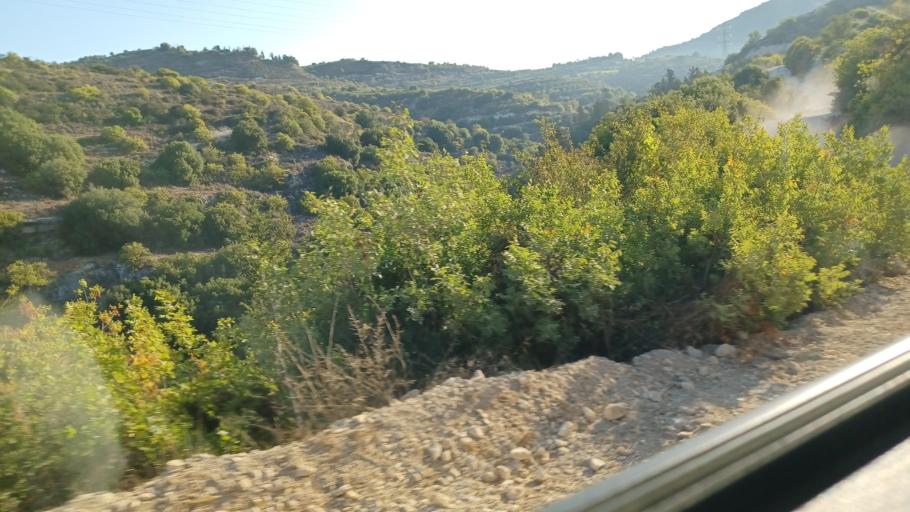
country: CY
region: Pafos
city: Tala
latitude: 34.8701
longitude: 32.4678
